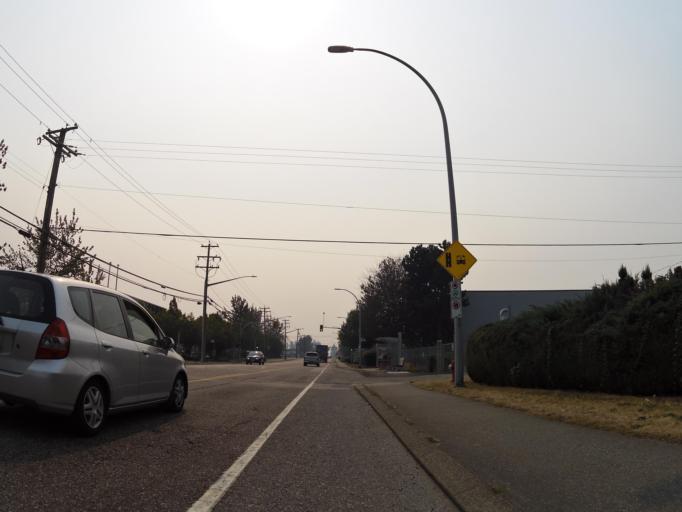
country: CA
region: British Columbia
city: Surrey
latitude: 49.1436
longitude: -122.8568
